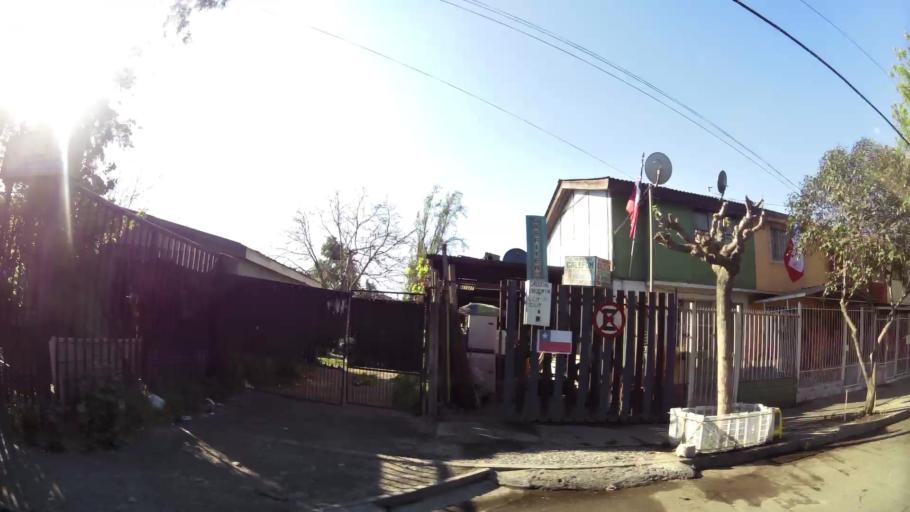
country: CL
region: Santiago Metropolitan
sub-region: Provincia de Santiago
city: La Pintana
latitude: -33.5473
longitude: -70.6305
